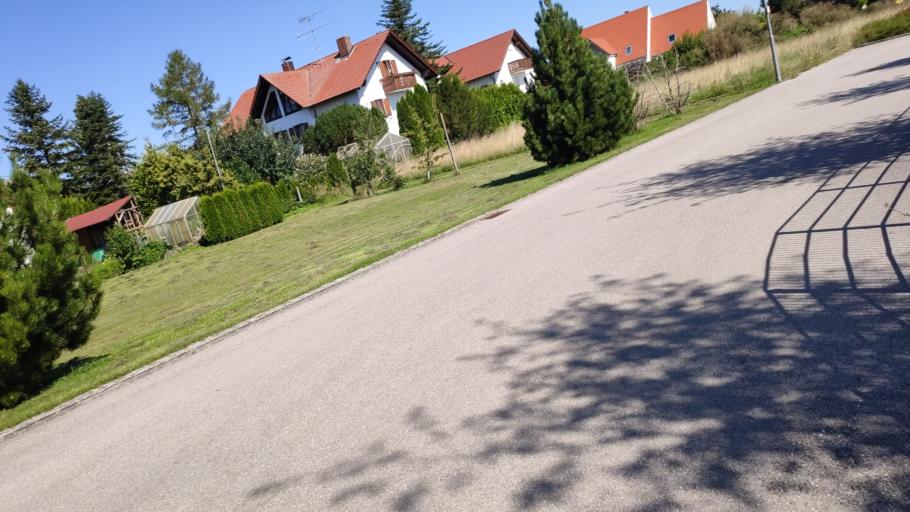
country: DE
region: Bavaria
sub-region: Swabia
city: Kleinaitingen
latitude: 48.2201
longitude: 10.8461
